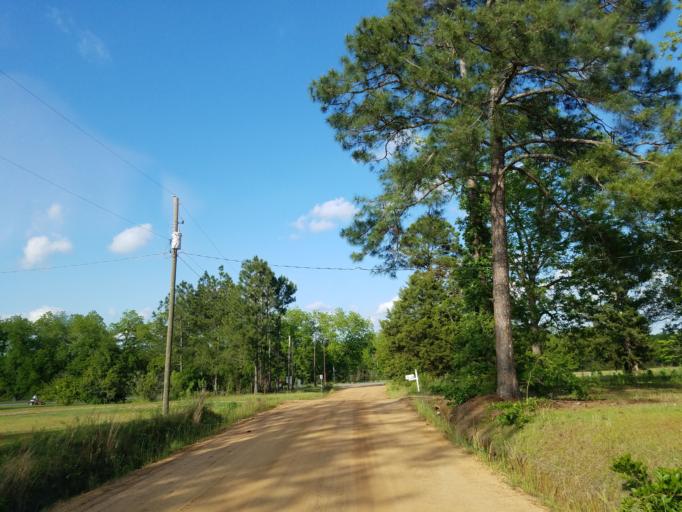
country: US
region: Georgia
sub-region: Turner County
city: Ashburn
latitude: 31.7744
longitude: -83.6933
